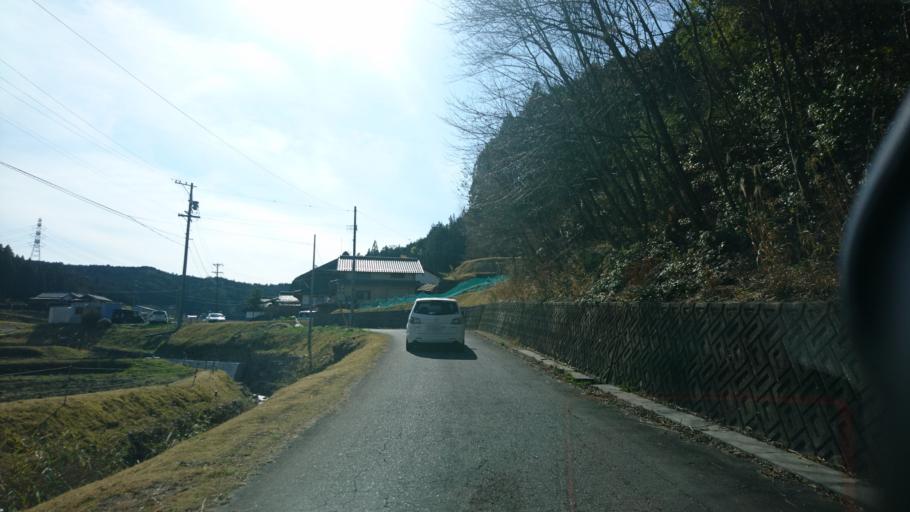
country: JP
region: Gifu
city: Mizunami
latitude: 35.4632
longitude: 137.3493
